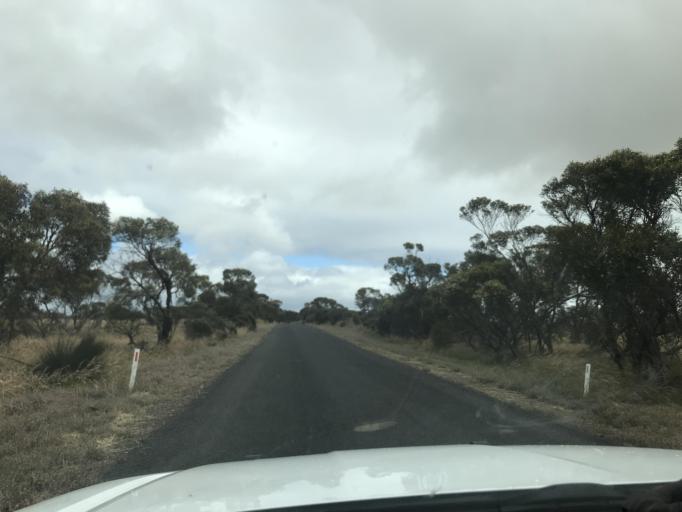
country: AU
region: South Australia
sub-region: Tatiara
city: Bordertown
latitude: -36.1333
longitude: 141.1671
